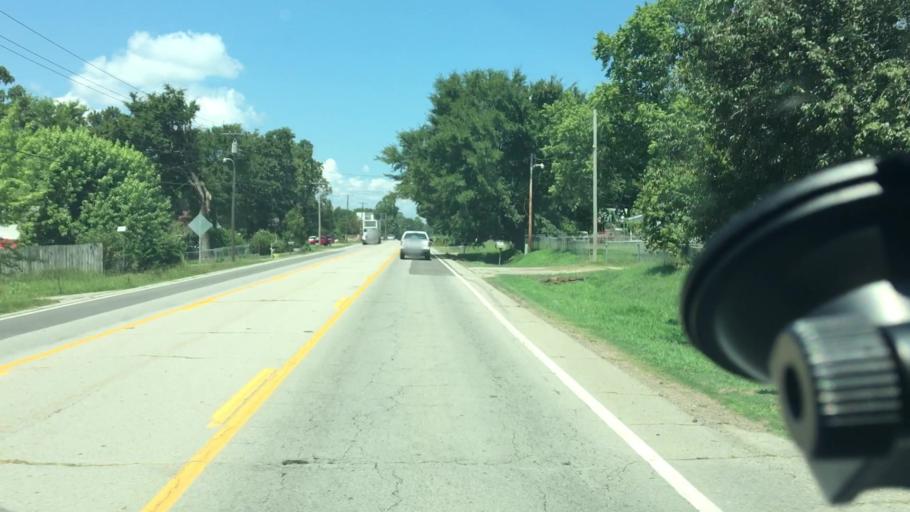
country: US
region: Arkansas
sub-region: Sebastian County
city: Lavaca
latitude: 35.2932
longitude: -94.1360
